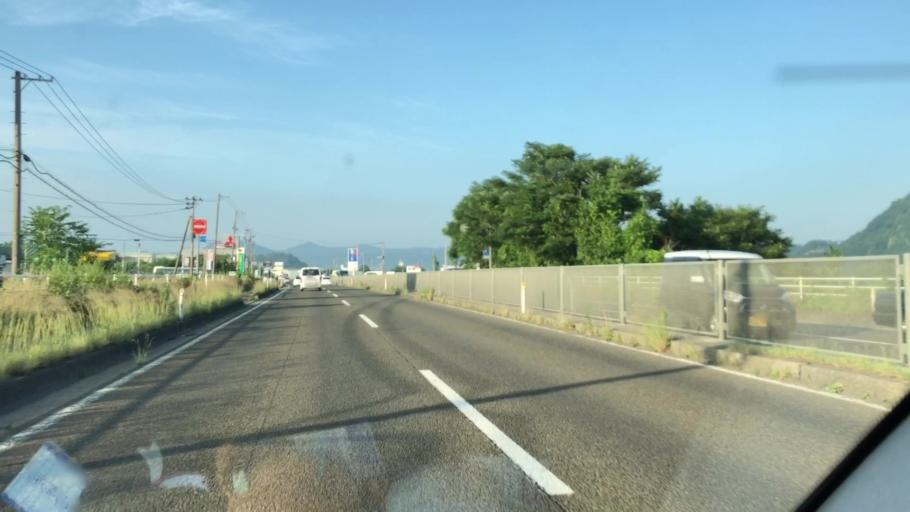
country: JP
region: Miyagi
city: Shiroishi
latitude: 38.0322
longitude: 140.6348
